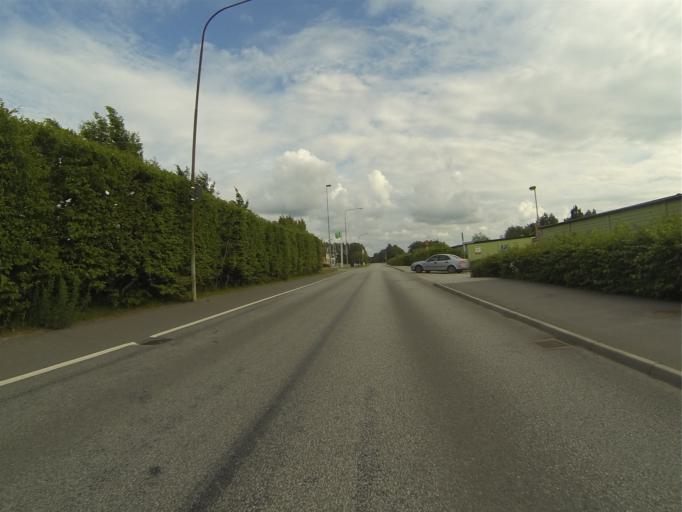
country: SE
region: Skane
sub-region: Staffanstorps Kommun
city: Staffanstorp
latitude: 55.6520
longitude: 13.2217
